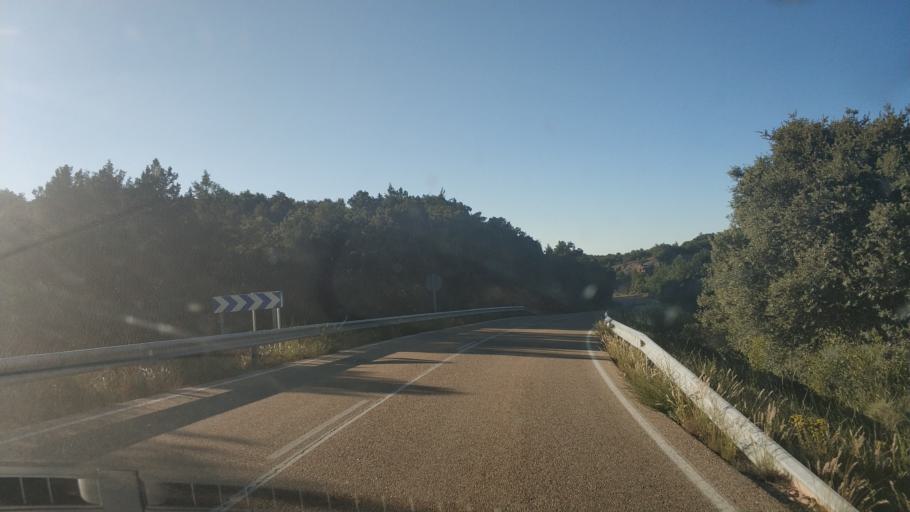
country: ES
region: Castille and Leon
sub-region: Provincia de Soria
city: Montejo de Tiermes
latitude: 41.4172
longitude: -3.2043
